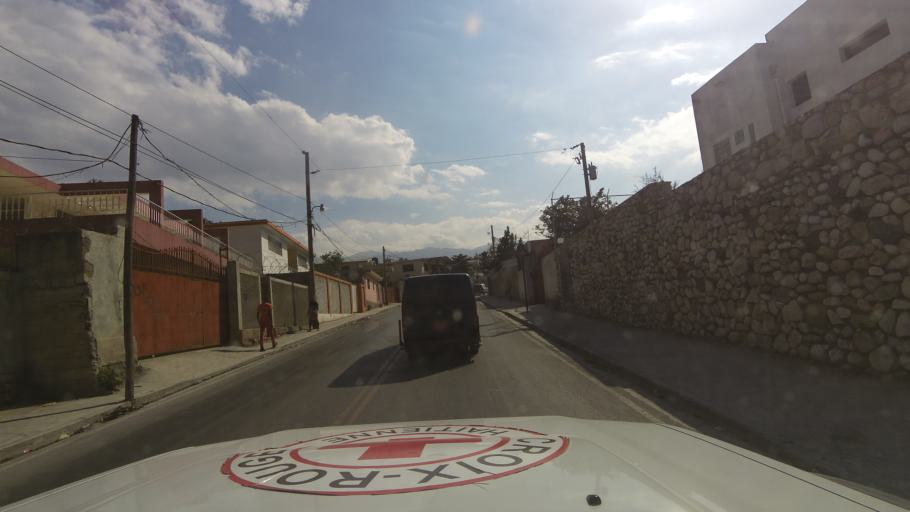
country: HT
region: Ouest
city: Delmas 73
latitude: 18.5355
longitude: -72.2871
